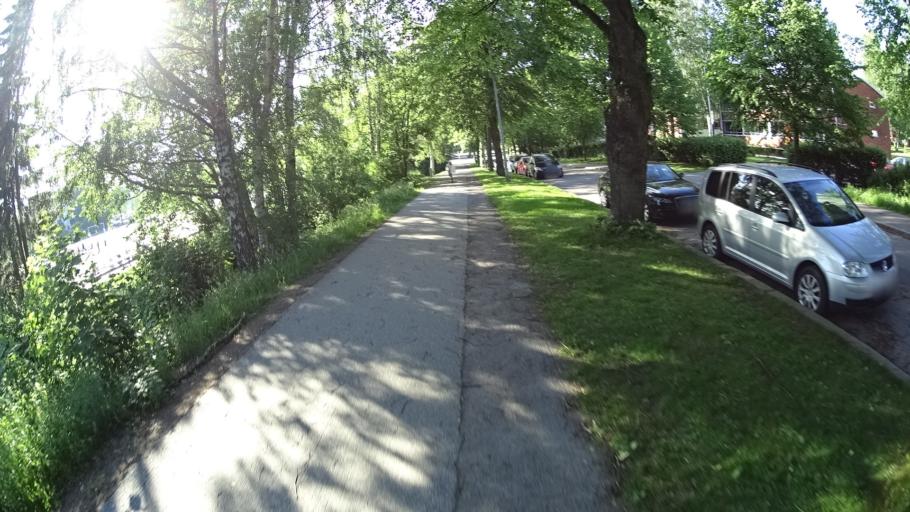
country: FI
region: Uusimaa
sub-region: Helsinki
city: Vantaa
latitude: 60.2149
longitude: 25.0988
